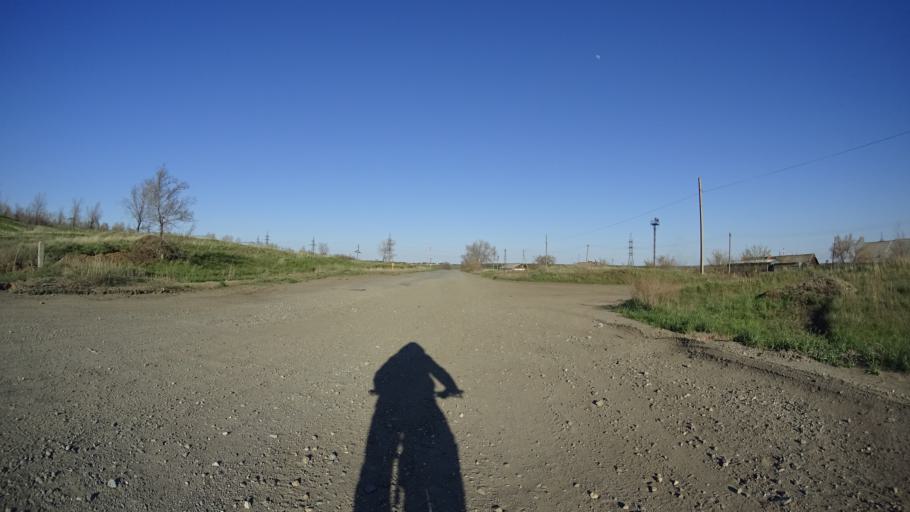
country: RU
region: Chelyabinsk
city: Troitsk
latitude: 54.0768
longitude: 61.6026
